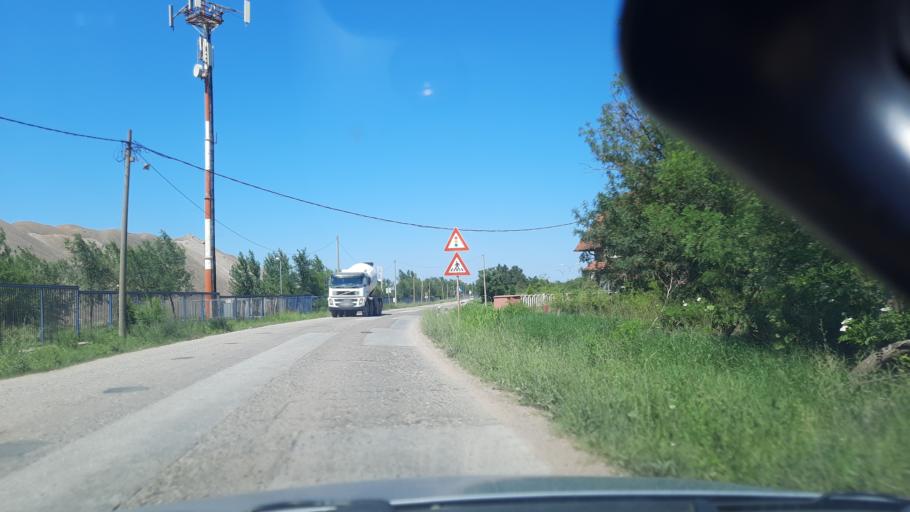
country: RS
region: Central Serbia
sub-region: Podunavski Okrug
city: Smederevo
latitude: 44.5940
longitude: 20.9841
